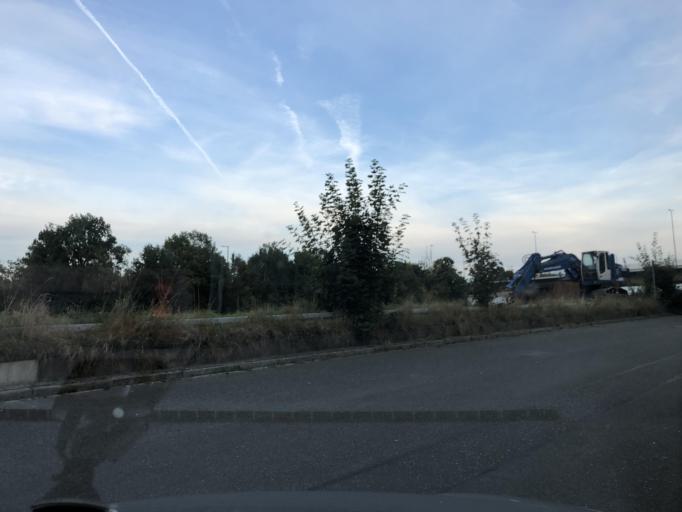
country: DE
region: Bavaria
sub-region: Regierungsbezirk Mittelfranken
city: Grossreuth bei Schweinau
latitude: 49.4397
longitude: 11.0005
